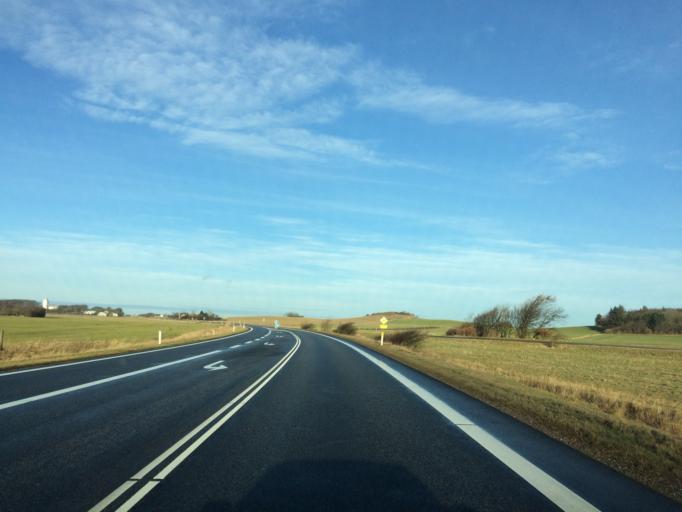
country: DK
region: Central Jutland
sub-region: Struer Kommune
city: Struer
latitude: 56.5185
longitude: 8.5717
